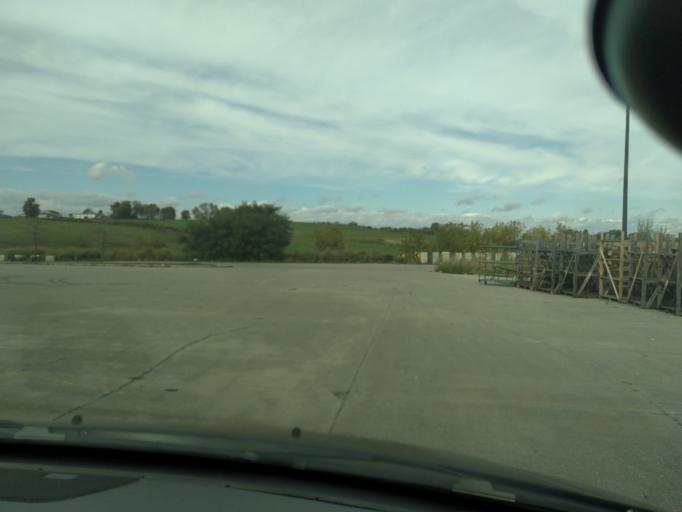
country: CA
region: Ontario
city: Newmarket
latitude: 44.0775
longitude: -79.4805
